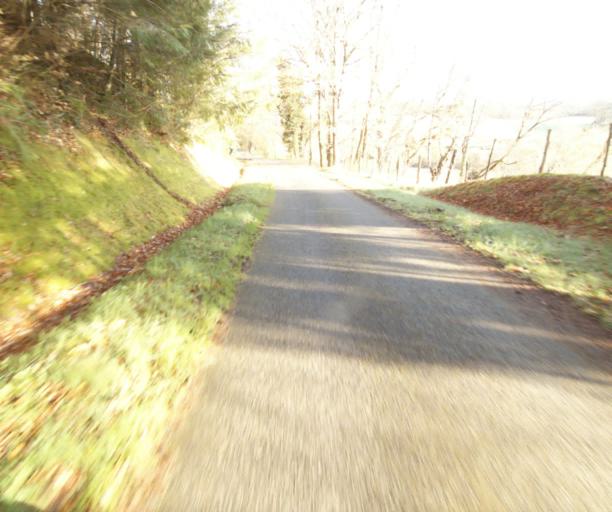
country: FR
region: Limousin
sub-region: Departement de la Correze
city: Correze
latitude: 45.2942
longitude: 1.8560
